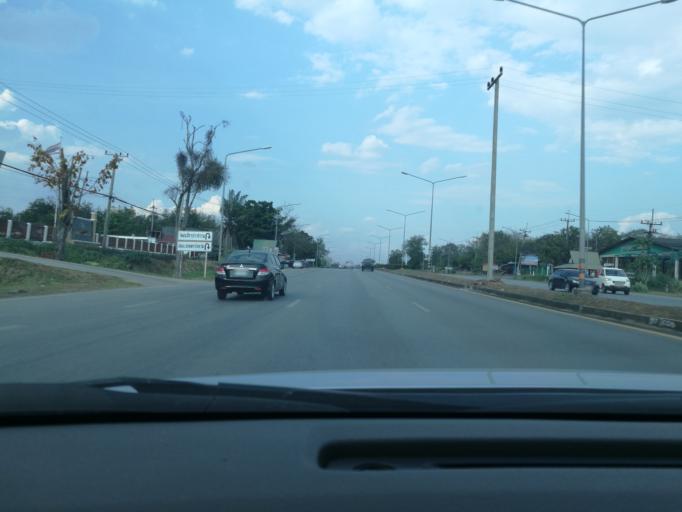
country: TH
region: Phetchabun
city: Phetchabun
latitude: 16.4622
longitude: 101.1563
